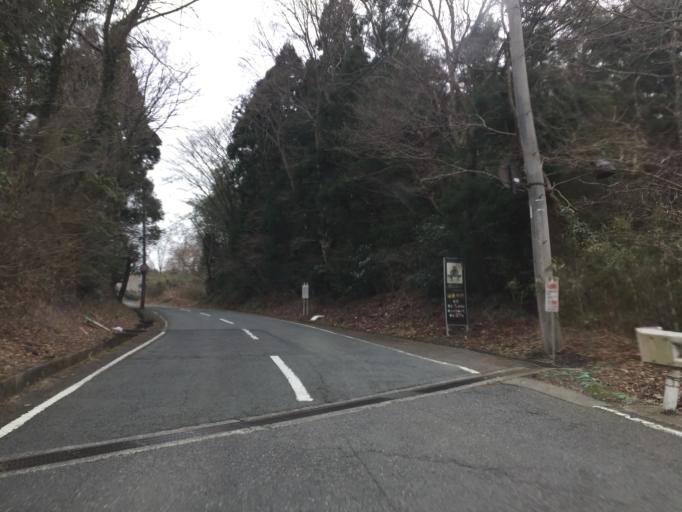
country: JP
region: Ibaraki
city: Kitaibaraki
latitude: 36.8764
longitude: 140.7837
